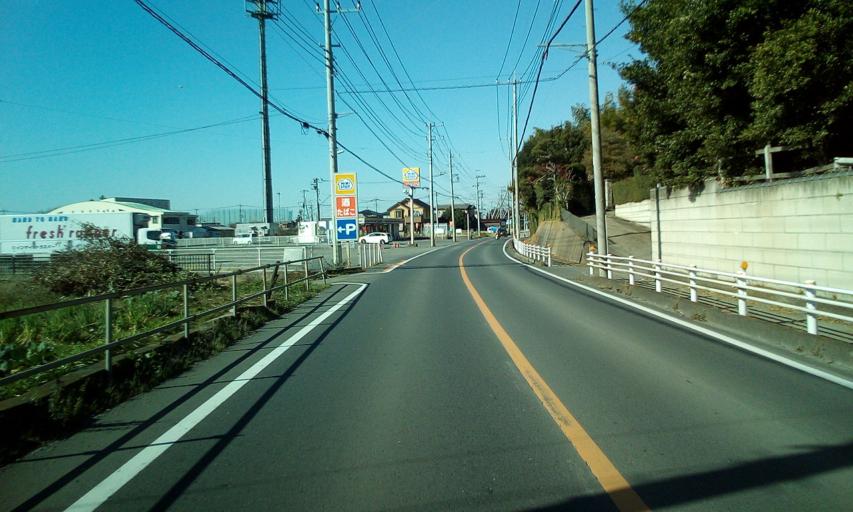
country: JP
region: Chiba
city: Noda
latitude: 35.9738
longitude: 139.8069
